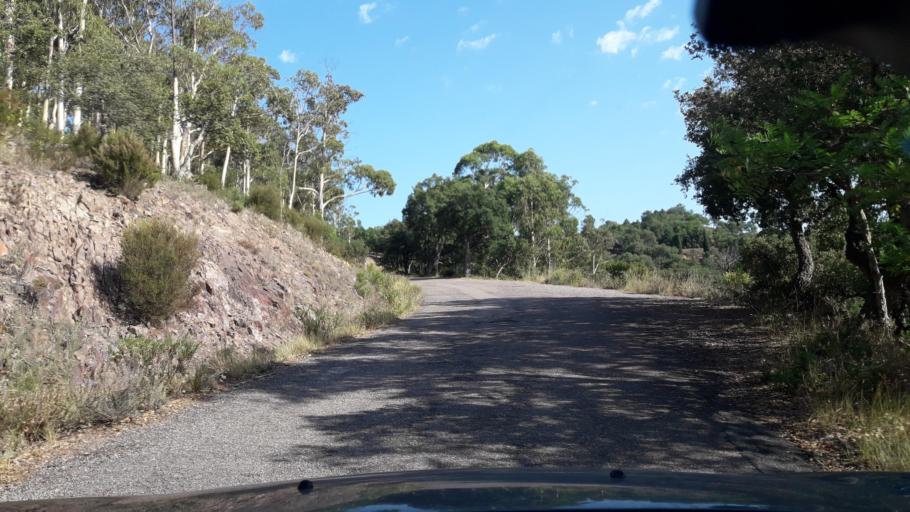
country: FR
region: Provence-Alpes-Cote d'Azur
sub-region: Departement du Var
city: Saint-Raphael
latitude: 43.4977
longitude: 6.8005
